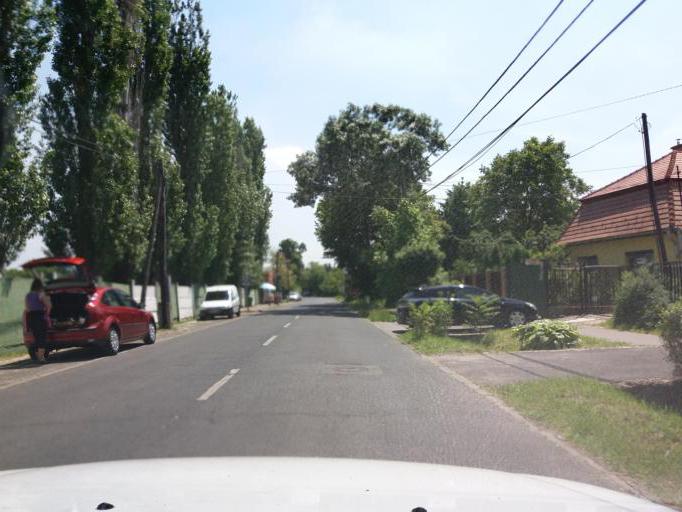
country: HU
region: Budapest
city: Budapest XXII. keruelet
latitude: 47.4484
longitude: 19.0248
